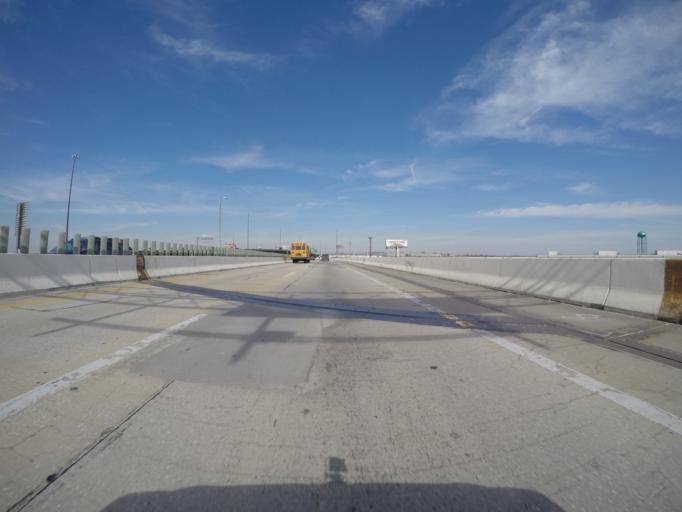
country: US
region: Maryland
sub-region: Baltimore County
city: Dundalk
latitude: 39.2671
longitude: -76.5596
